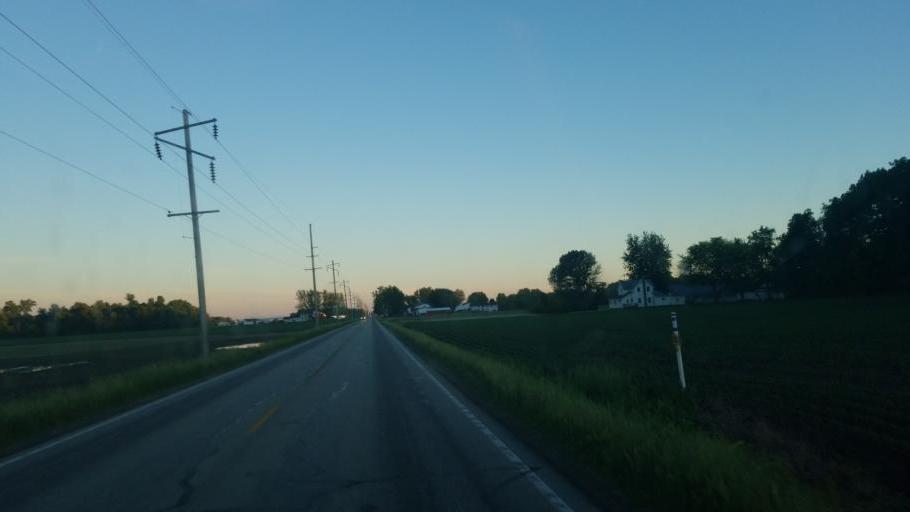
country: US
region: Indiana
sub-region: Elkhart County
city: Nappanee
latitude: 41.3883
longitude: -86.0009
